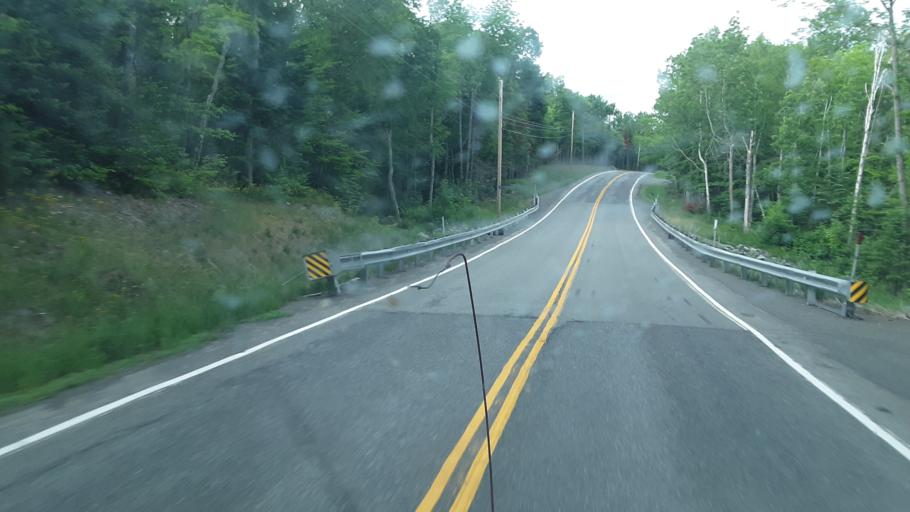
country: US
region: Maine
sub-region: Penobscot County
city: Patten
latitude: 46.1368
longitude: -68.3757
